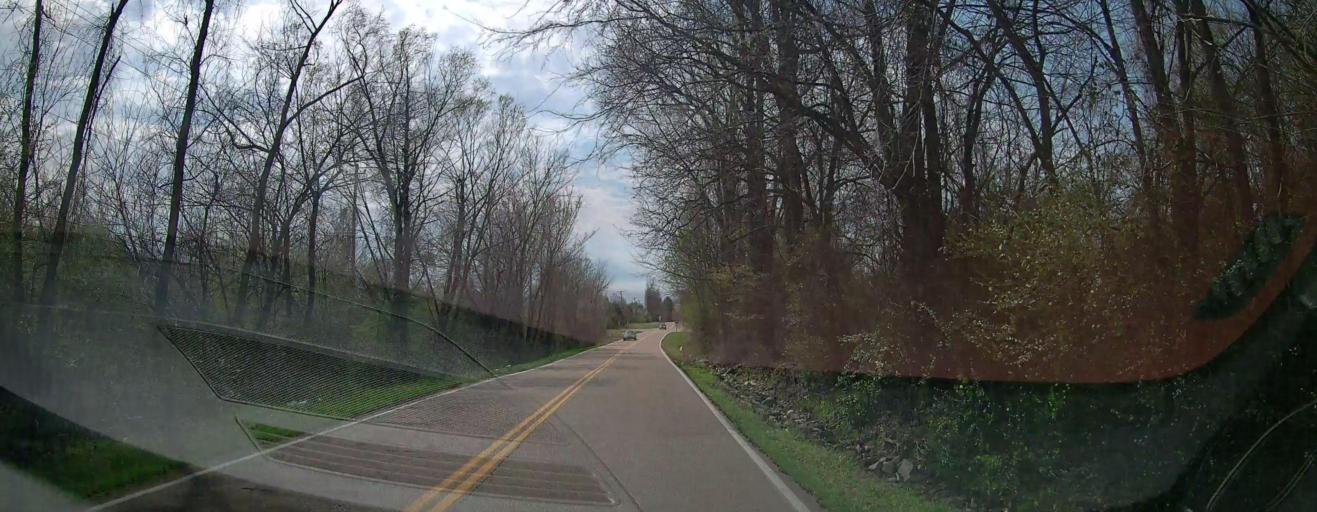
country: US
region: Mississippi
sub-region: De Soto County
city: Olive Branch
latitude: 35.0042
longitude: -89.8485
